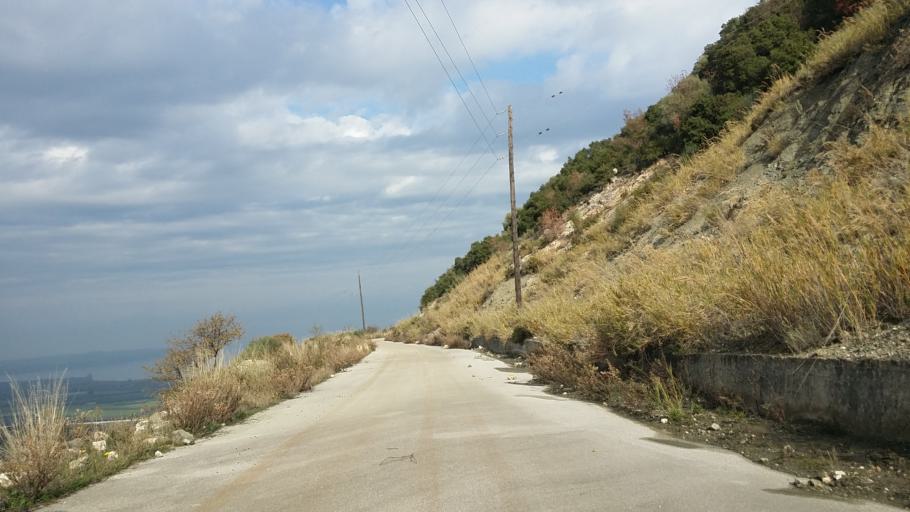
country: GR
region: West Greece
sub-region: Nomos Aitolias kai Akarnanias
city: Katouna
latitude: 38.8562
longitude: 21.0559
